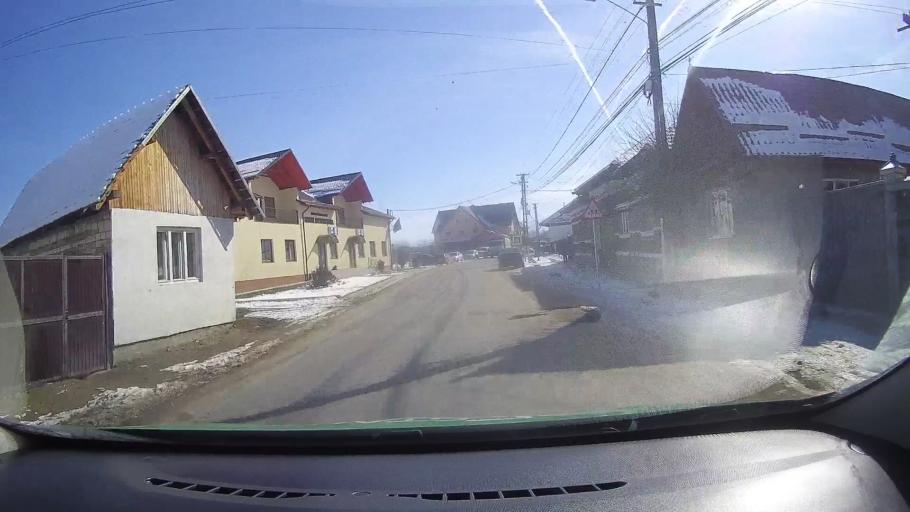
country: RO
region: Brasov
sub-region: Comuna Sambata de Sus
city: Sambata de Sus
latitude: 45.7604
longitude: 24.8238
